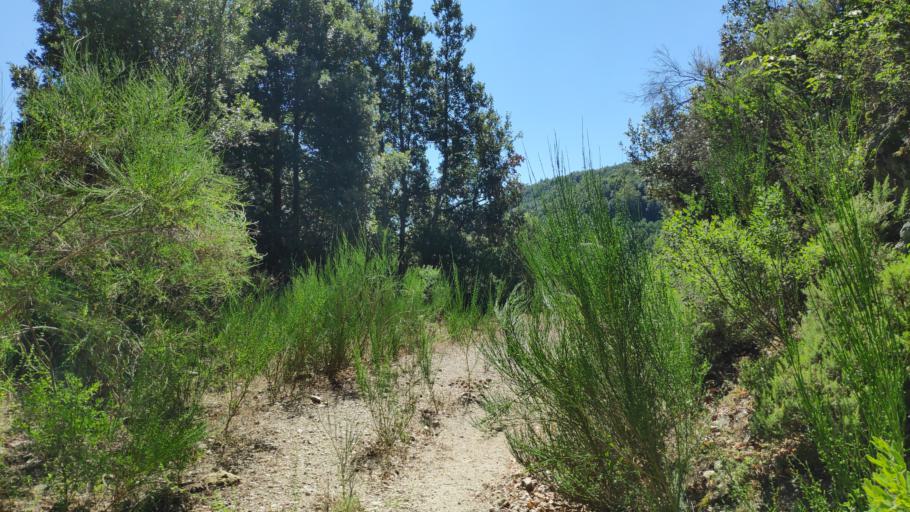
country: IT
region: Calabria
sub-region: Provincia di Vibo-Valentia
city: Nardodipace
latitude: 38.4823
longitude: 16.3816
